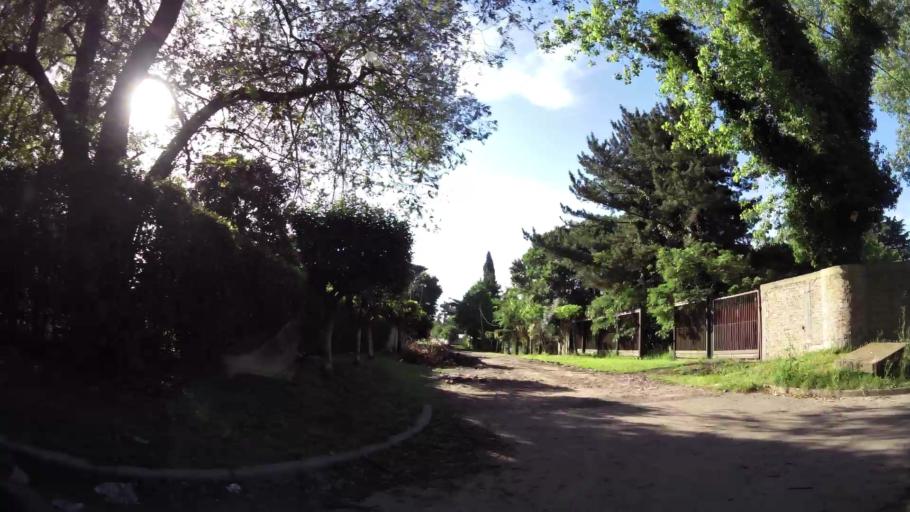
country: AR
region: Buenos Aires
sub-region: Partido de Quilmes
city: Quilmes
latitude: -34.8173
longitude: -58.2161
